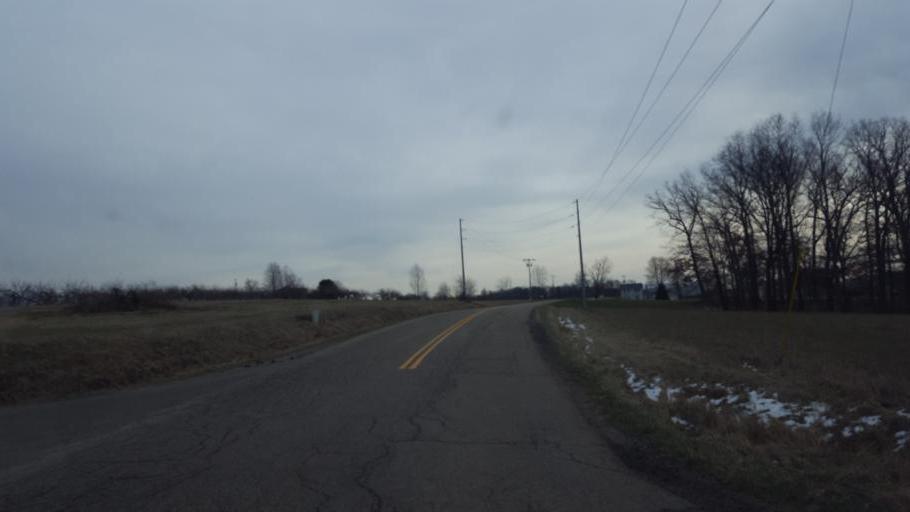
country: US
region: Ohio
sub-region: Knox County
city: Fredericktown
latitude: 40.4980
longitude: -82.4481
